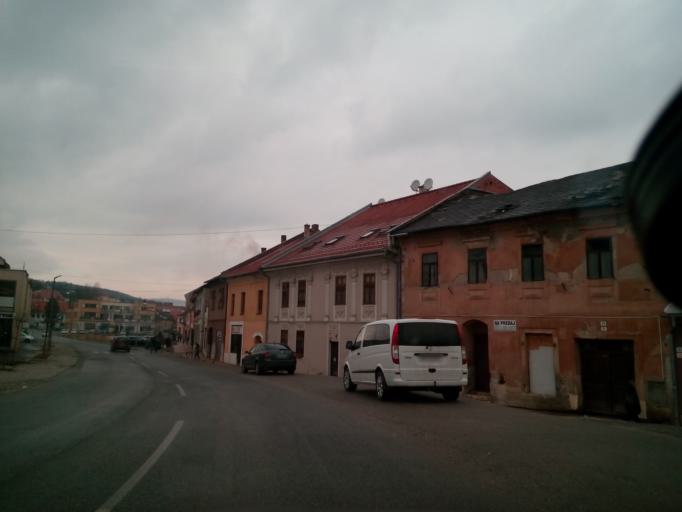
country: SK
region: Presovsky
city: Spisske Podhradie
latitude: 48.9995
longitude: 20.7548
